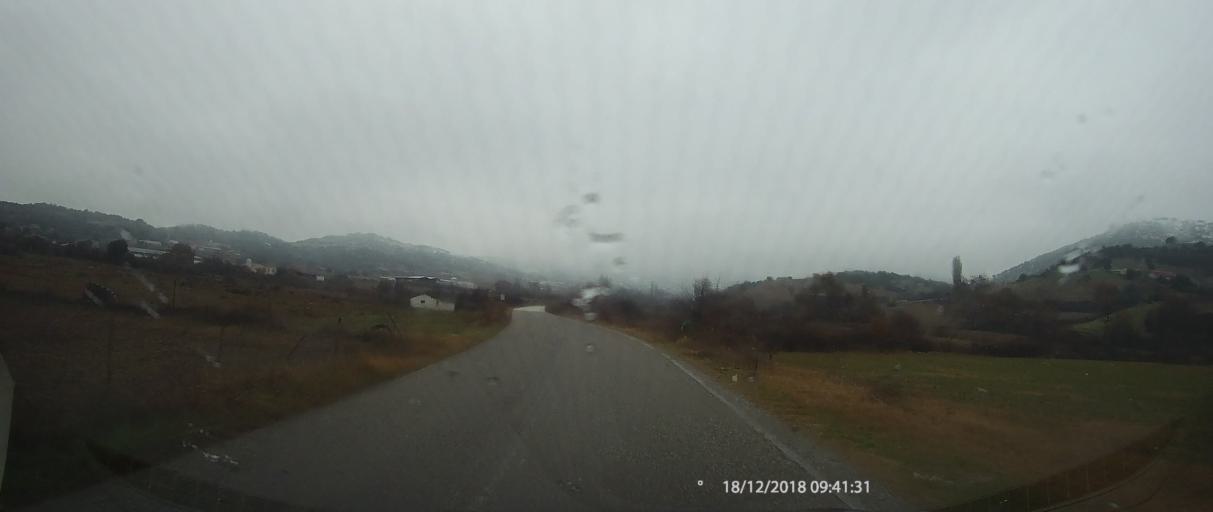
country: GR
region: Thessaly
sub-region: Nomos Larisis
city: Elassona
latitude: 40.0125
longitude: 22.2324
